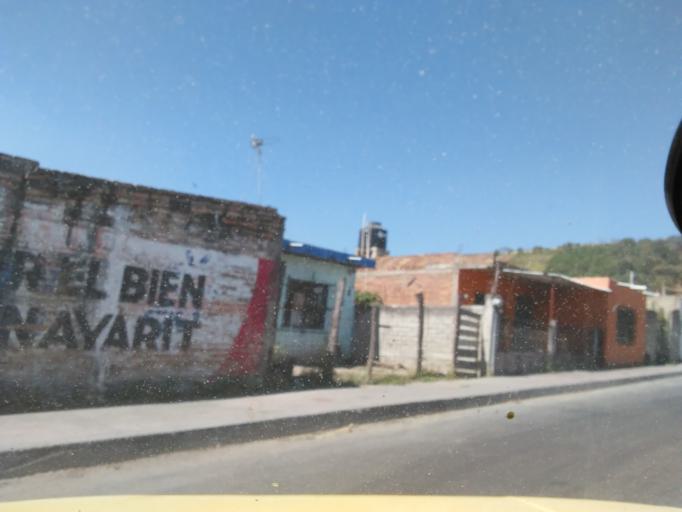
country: MX
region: Nayarit
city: Xalisco
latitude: 21.4383
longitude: -104.8981
